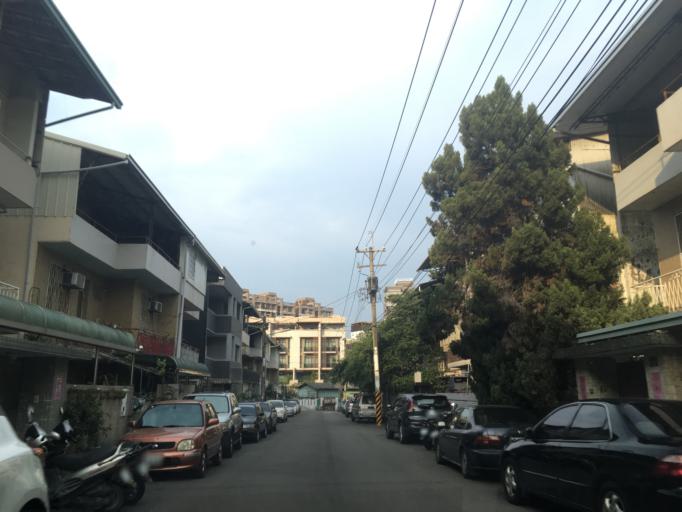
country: TW
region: Taiwan
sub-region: Taichung City
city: Taichung
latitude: 24.1724
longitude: 120.7322
